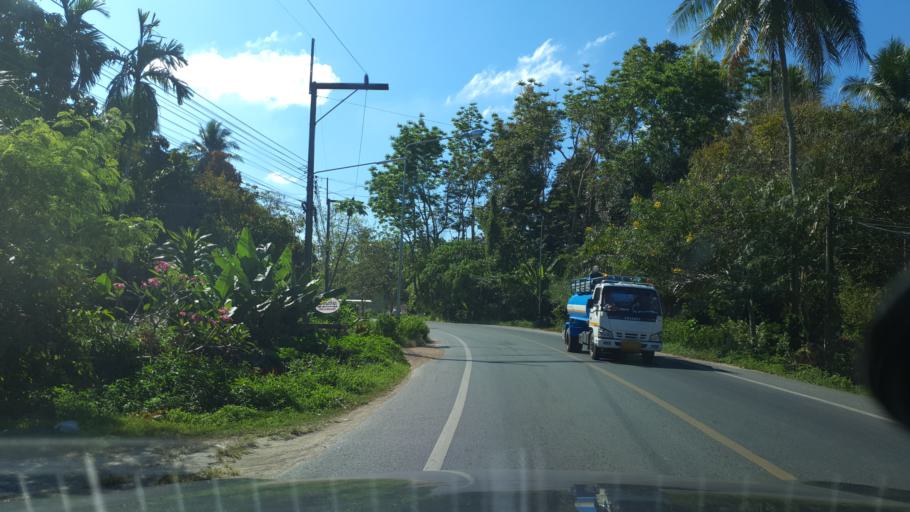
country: TH
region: Phangnga
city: Ban Ao Nang
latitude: 8.0661
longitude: 98.8093
